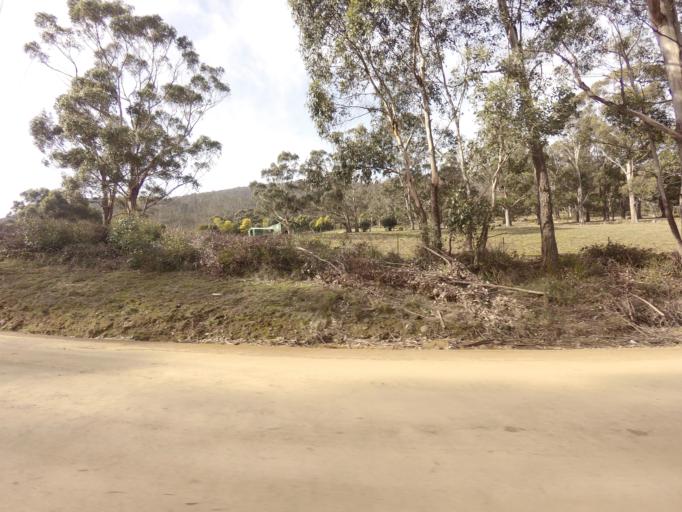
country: AU
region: Tasmania
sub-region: Huon Valley
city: Huonville
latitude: -43.0715
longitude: 147.0841
